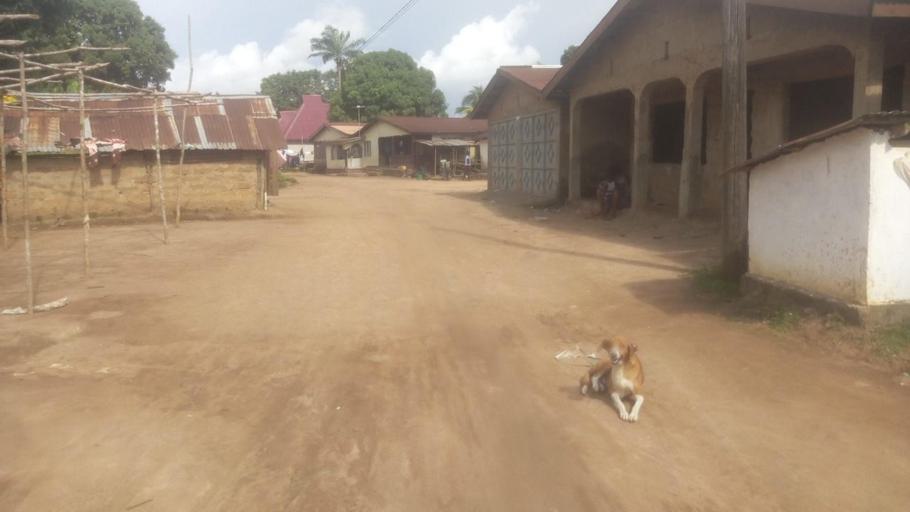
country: SL
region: Northern Province
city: Masoyila
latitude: 8.6099
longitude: -13.1910
